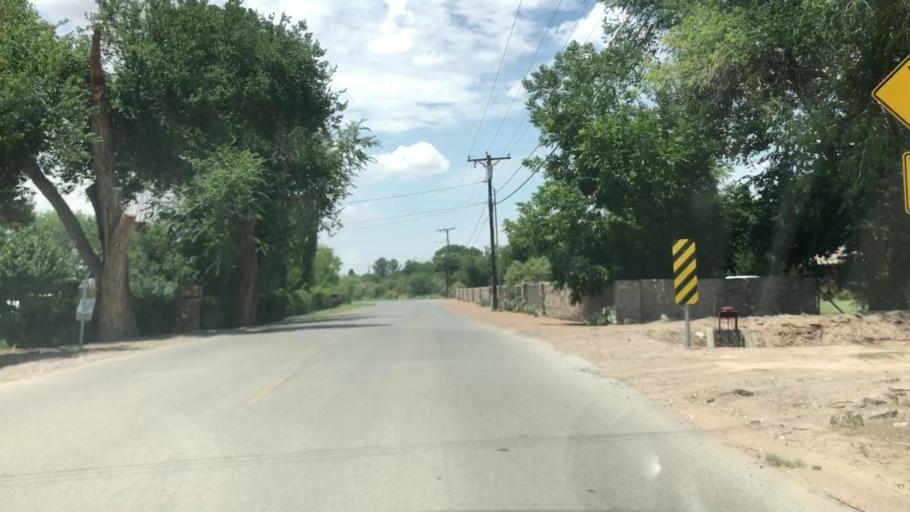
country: US
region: Texas
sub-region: El Paso County
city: Canutillo
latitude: 31.9090
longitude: -106.6334
